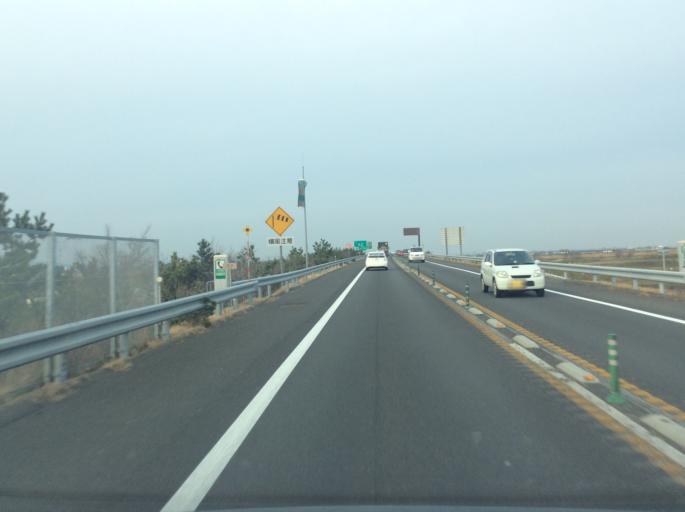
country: JP
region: Miyagi
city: Iwanuma
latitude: 38.0906
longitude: 140.8870
